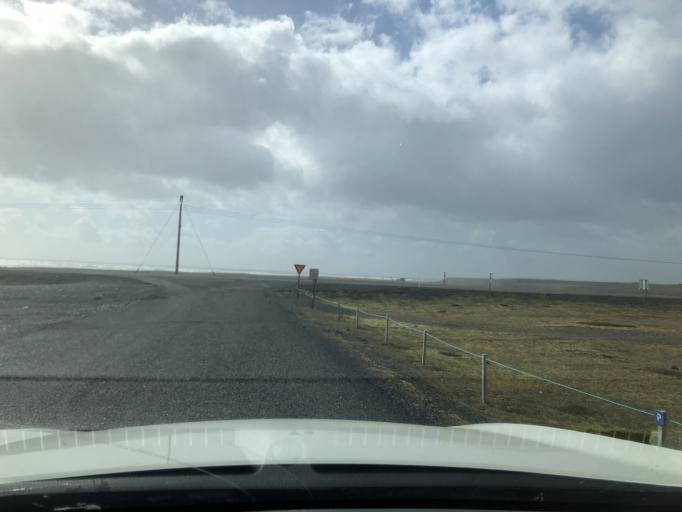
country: IS
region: East
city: Hoefn
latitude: 64.0455
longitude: -16.1836
